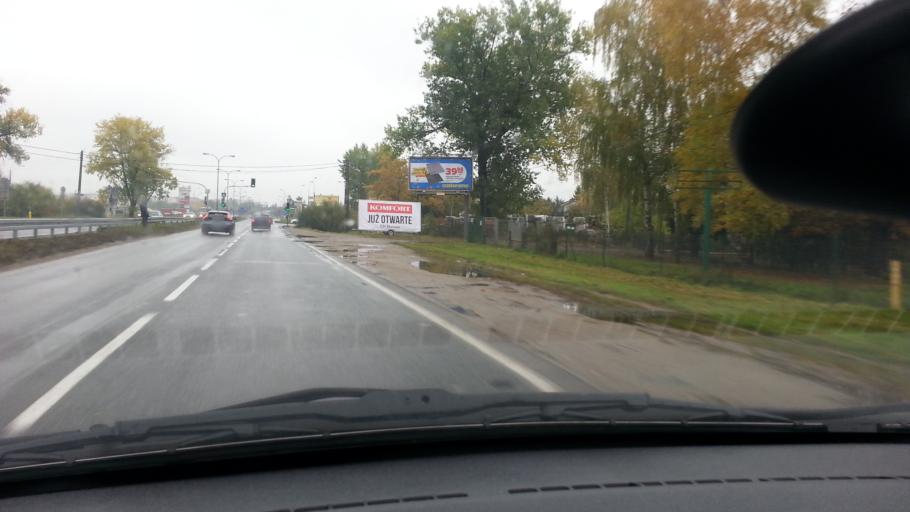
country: PL
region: Masovian Voivodeship
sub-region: Powiat pruszkowski
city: Michalowice
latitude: 52.1818
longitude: 20.8924
